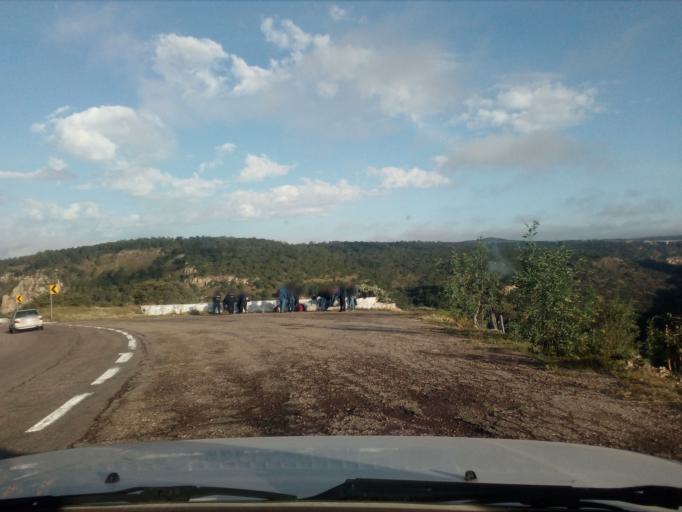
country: MX
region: Durango
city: Victoria de Durango
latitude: 23.9561
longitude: -104.8501
